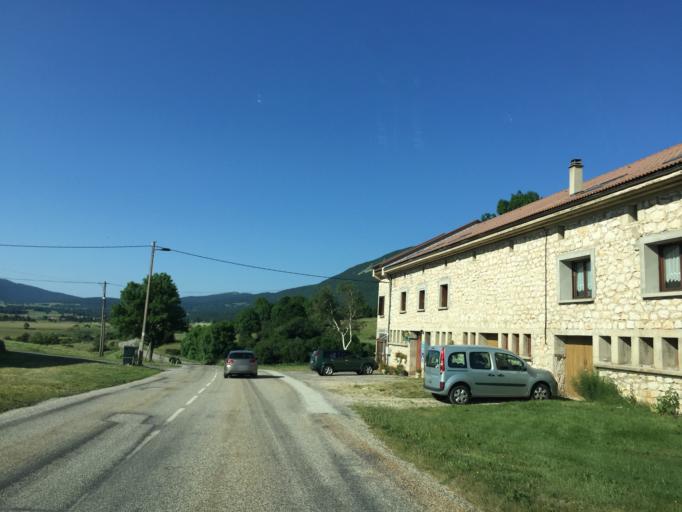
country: FR
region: Rhone-Alpes
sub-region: Departement de la Drome
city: Saint-Laurent-en-Royans
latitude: 44.9148
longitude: 5.3766
